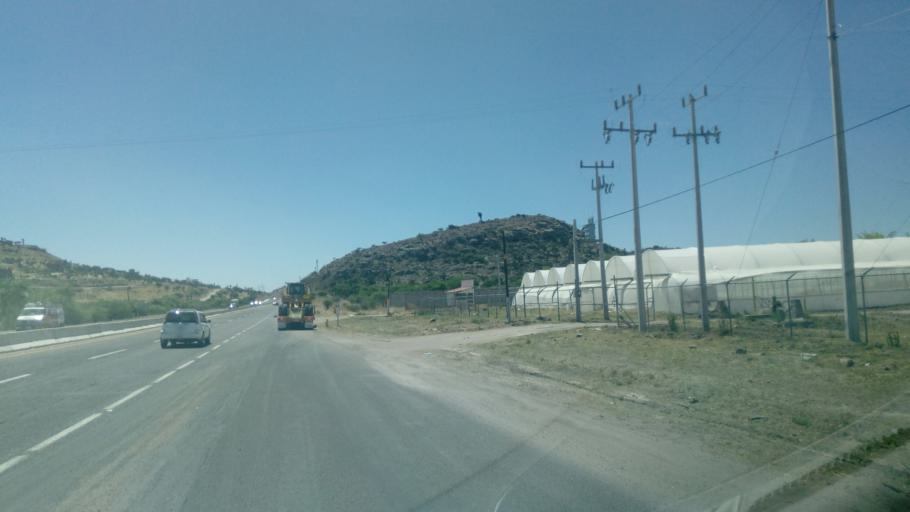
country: MX
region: Durango
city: Victoria de Durango
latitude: 24.0961
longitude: -104.6860
